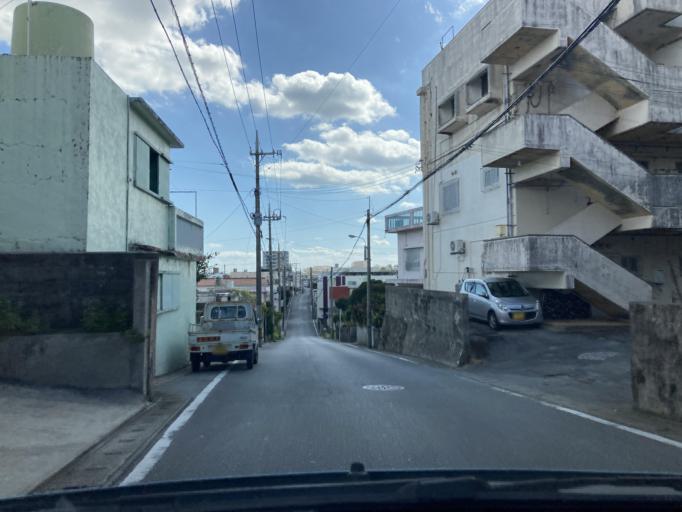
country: JP
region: Okinawa
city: Okinawa
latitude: 26.3423
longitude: 127.8059
